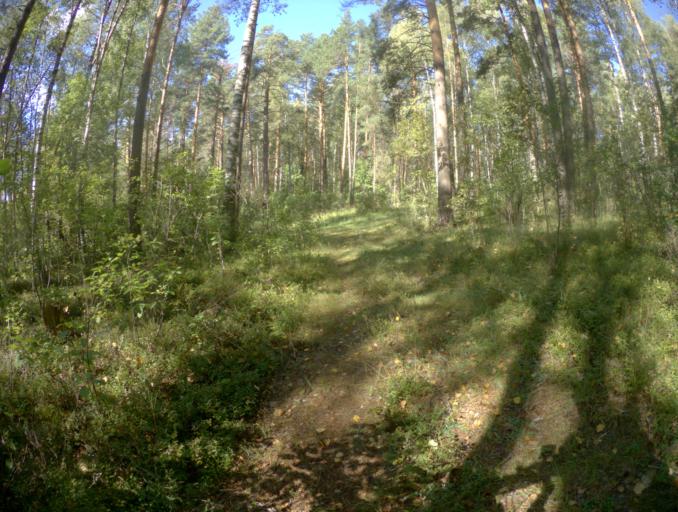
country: RU
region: Vladimir
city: Nikologory
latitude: 56.1080
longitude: 41.9017
